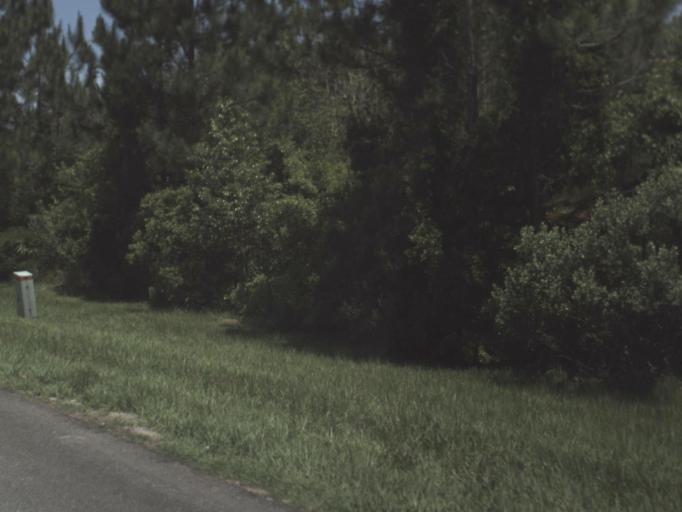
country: US
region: Florida
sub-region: Suwannee County
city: Live Oak
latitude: 30.3121
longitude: -83.0206
